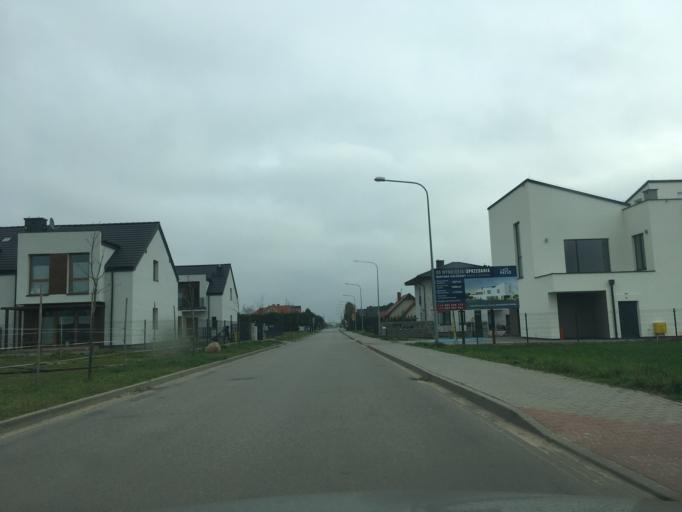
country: PL
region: Masovian Voivodeship
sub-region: Powiat piaseczynski
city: Lesznowola
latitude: 52.0845
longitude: 20.9433
